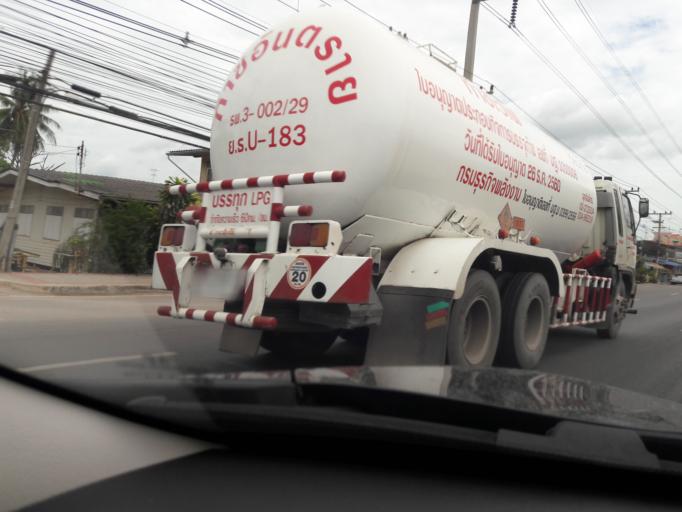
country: TH
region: Ratchaburi
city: Damnoen Saduak
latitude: 13.5548
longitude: 99.9680
